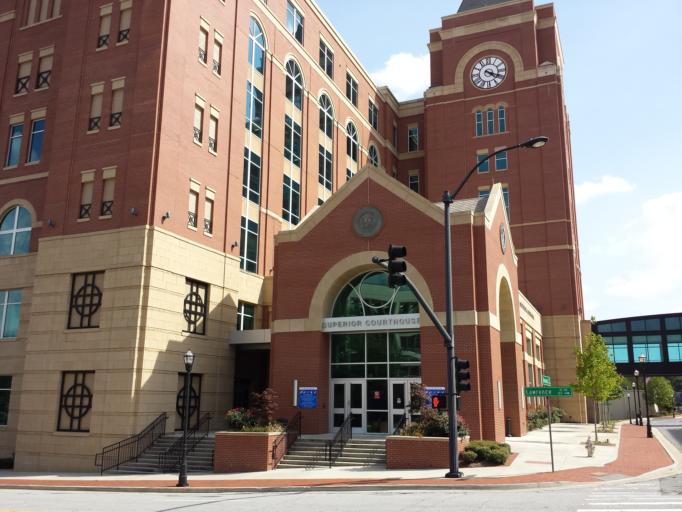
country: US
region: Georgia
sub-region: Cobb County
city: Marietta
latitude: 33.9534
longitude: -84.5470
